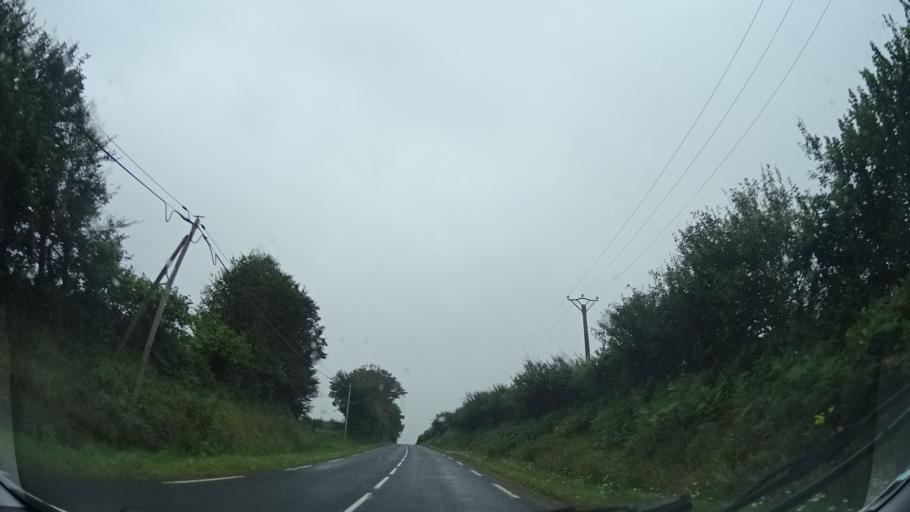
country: FR
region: Lower Normandy
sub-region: Departement de la Manche
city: Martinvast
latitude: 49.6142
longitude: -1.6941
